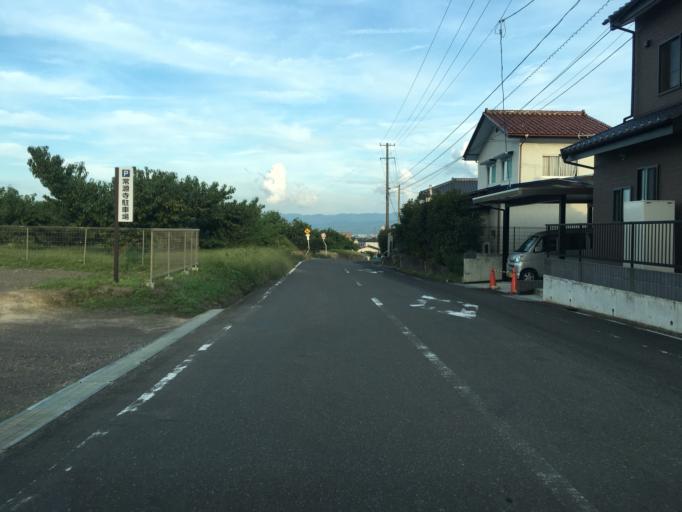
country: JP
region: Fukushima
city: Hobaramachi
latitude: 37.8586
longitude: 140.5165
